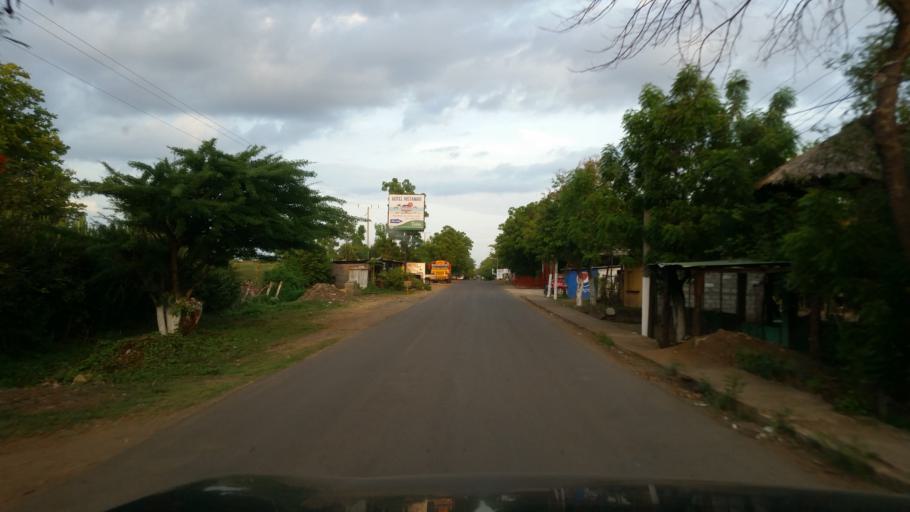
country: NI
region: Managua
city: Masachapa
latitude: 11.7789
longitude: -86.5121
